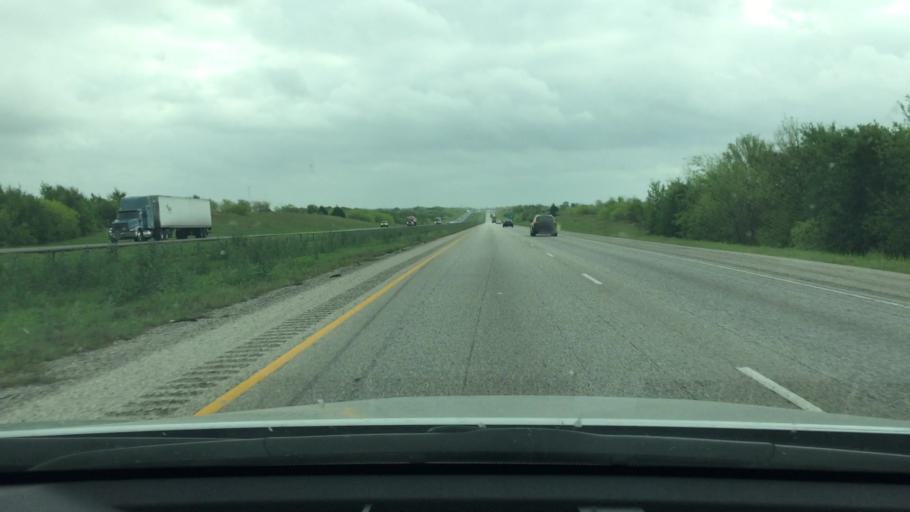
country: US
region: Texas
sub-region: Gonzales County
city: Waelder
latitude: 29.6668
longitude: -97.3313
